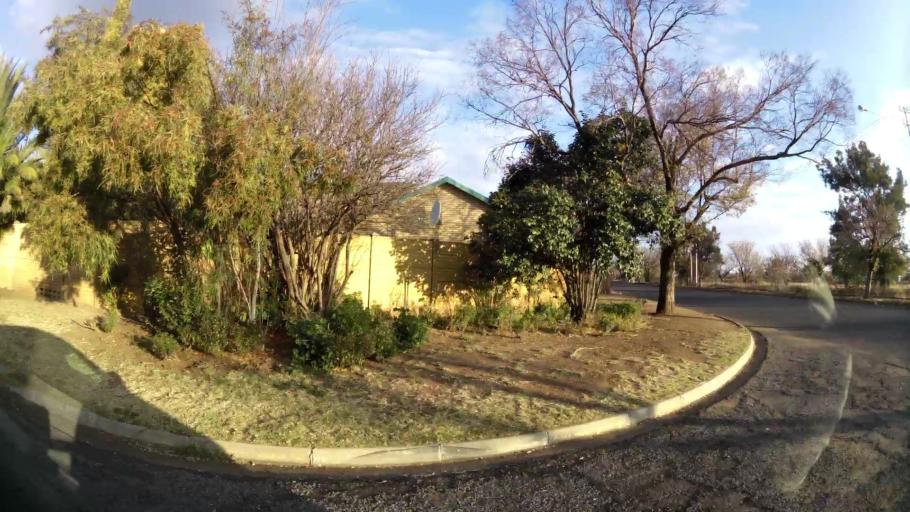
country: ZA
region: Orange Free State
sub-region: Mangaung Metropolitan Municipality
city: Bloemfontein
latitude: -29.1347
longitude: 26.1909
